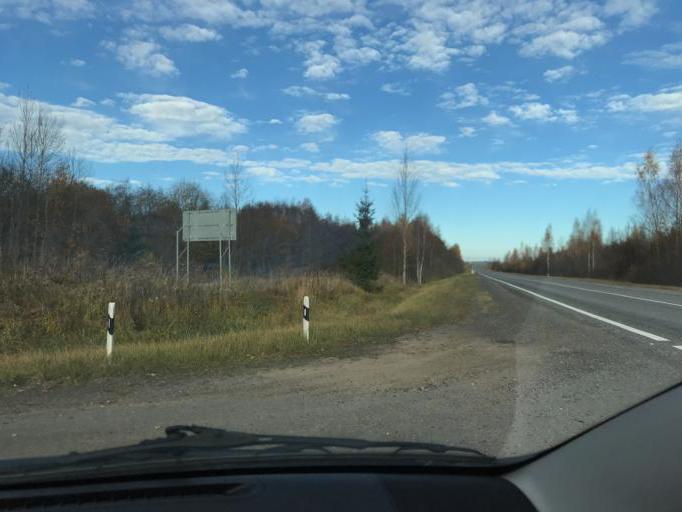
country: BY
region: Vitebsk
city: Haradok
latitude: 55.4581
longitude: 30.0443
